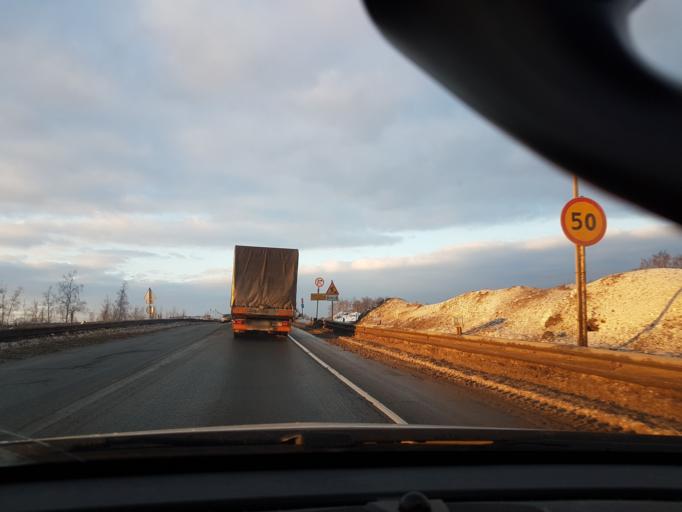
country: RU
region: Moskovskaya
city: Istra
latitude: 55.8973
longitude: 36.9447
